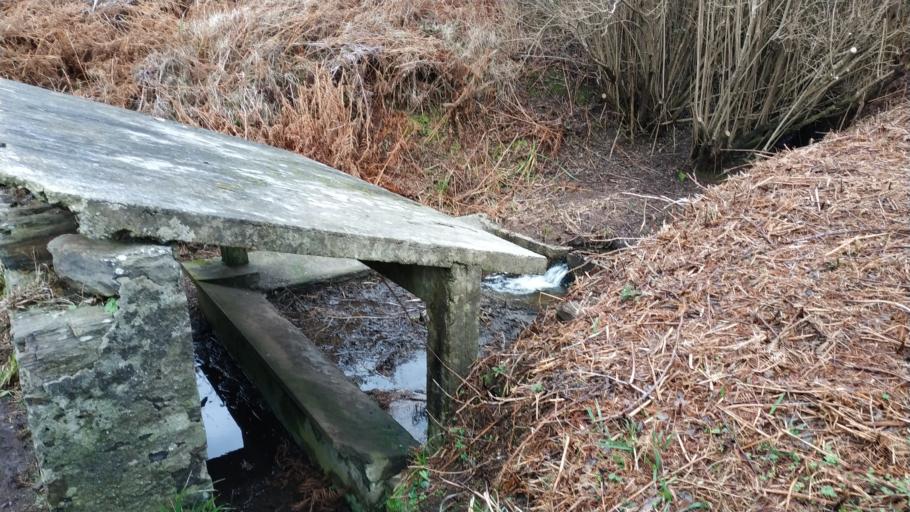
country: ES
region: Galicia
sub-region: Provincia da Coruna
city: Oleiros
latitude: 43.4006
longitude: -8.3296
